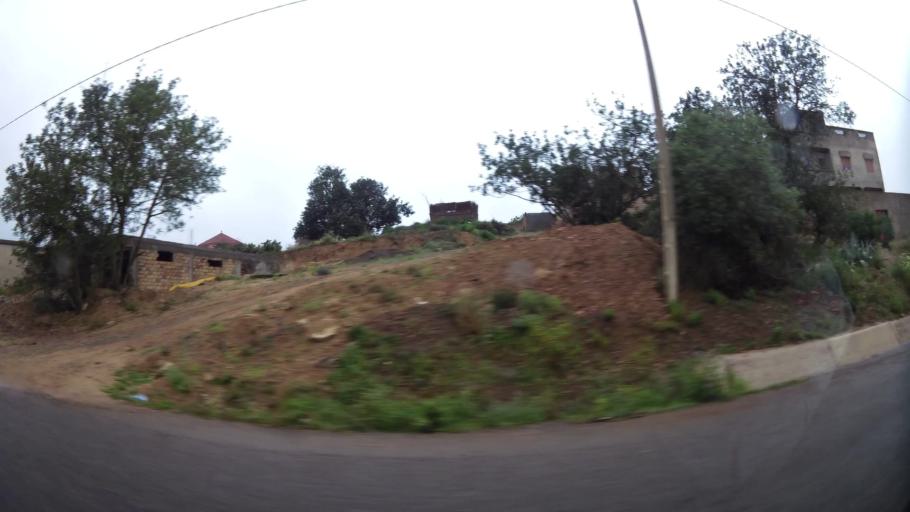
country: MA
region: Oriental
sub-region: Nador
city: Boudinar
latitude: 35.1319
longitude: -3.5903
